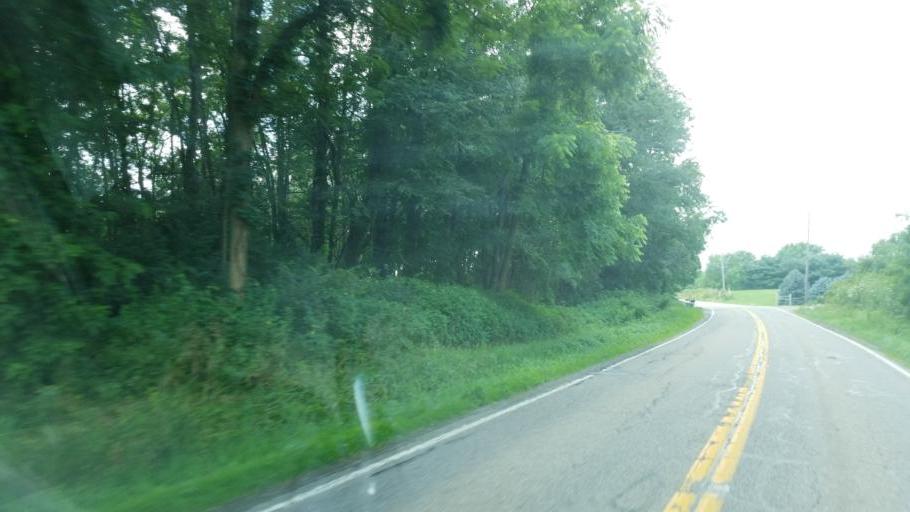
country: US
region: Ohio
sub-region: Stark County
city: Minerva
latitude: 40.7905
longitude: -81.0214
